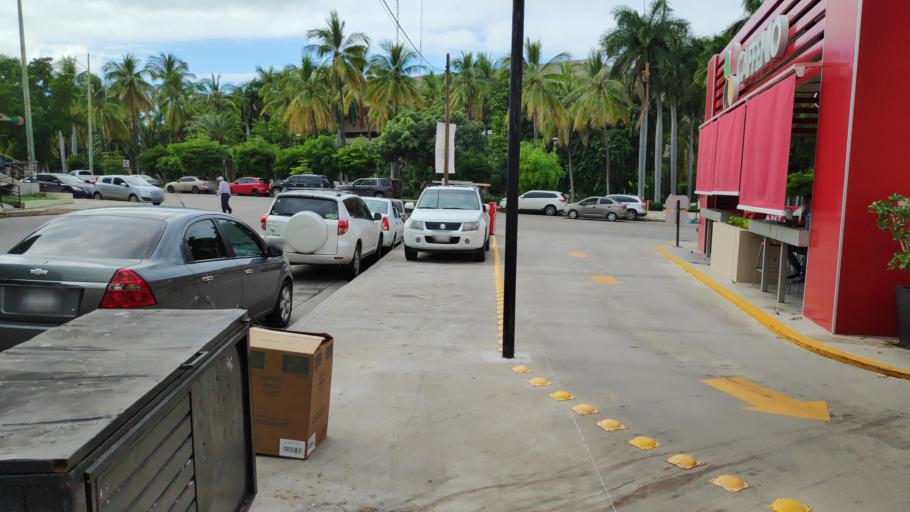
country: MX
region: Sinaloa
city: Culiacan
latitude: 24.7977
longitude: -107.4067
